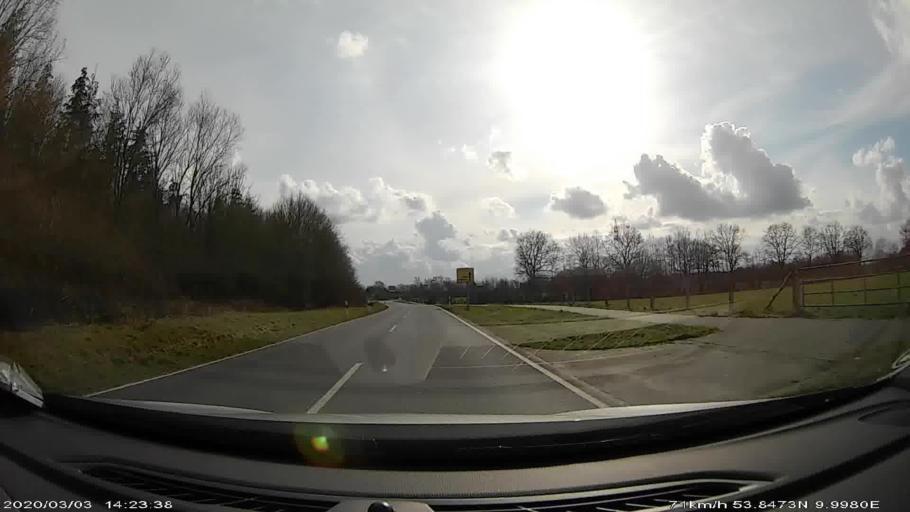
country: DE
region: Schleswig-Holstein
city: Kattendorf
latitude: 53.8470
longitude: 9.9978
